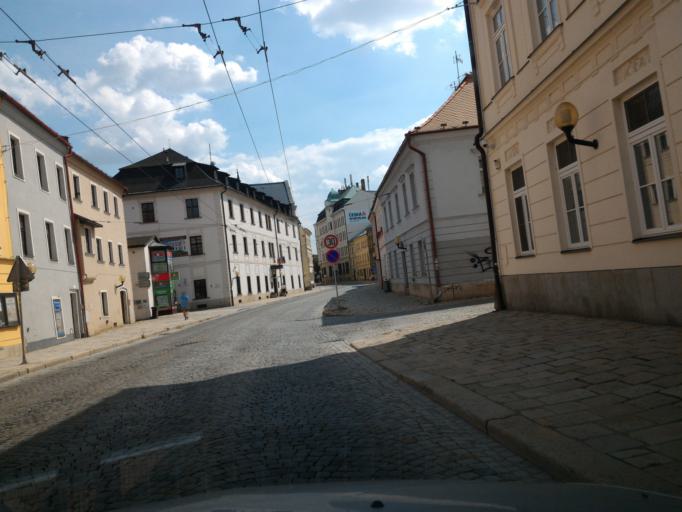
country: CZ
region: Vysocina
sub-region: Okres Jihlava
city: Jihlava
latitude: 49.3987
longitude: 15.5904
